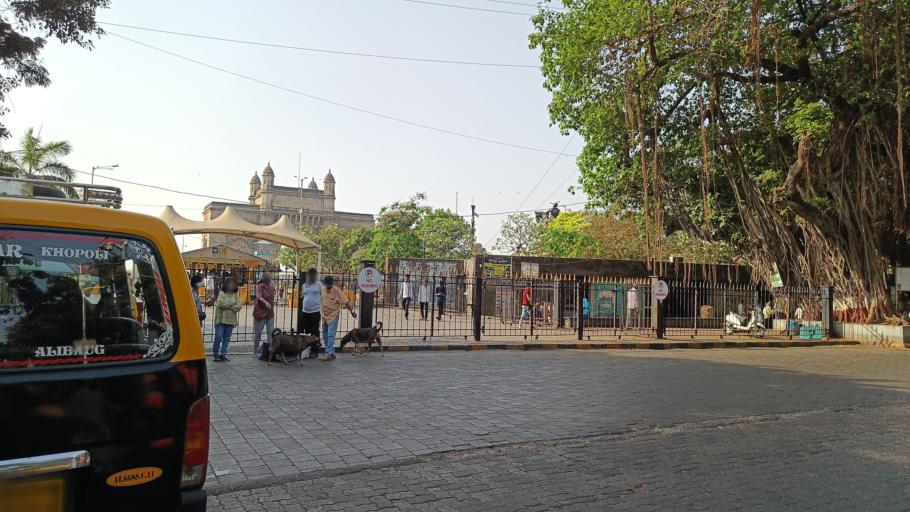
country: IN
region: Maharashtra
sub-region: Raigarh
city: Uran
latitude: 18.9234
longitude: 72.8339
